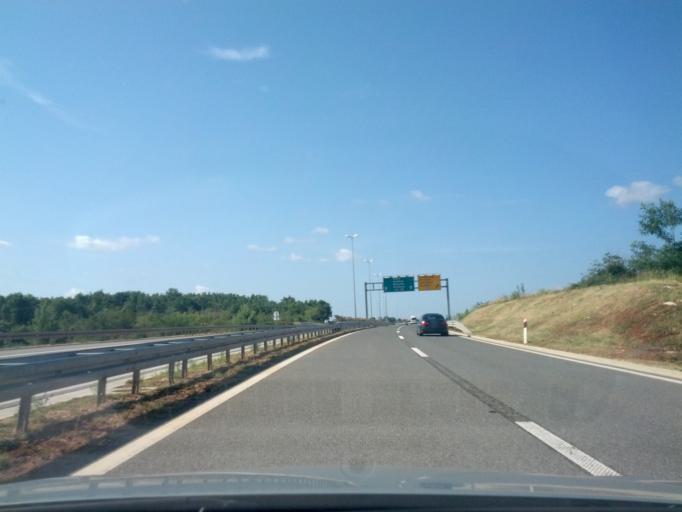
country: HR
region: Istarska
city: Buje
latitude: 45.4095
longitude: 13.6217
